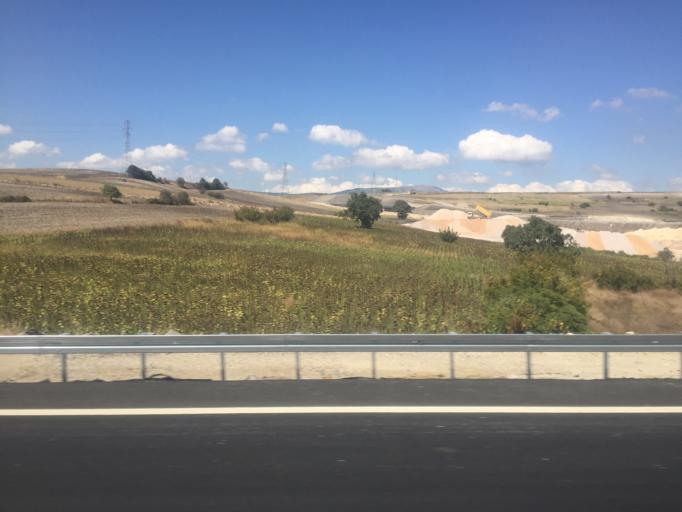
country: TR
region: Balikesir
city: Susurluk
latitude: 39.9662
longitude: 28.1637
